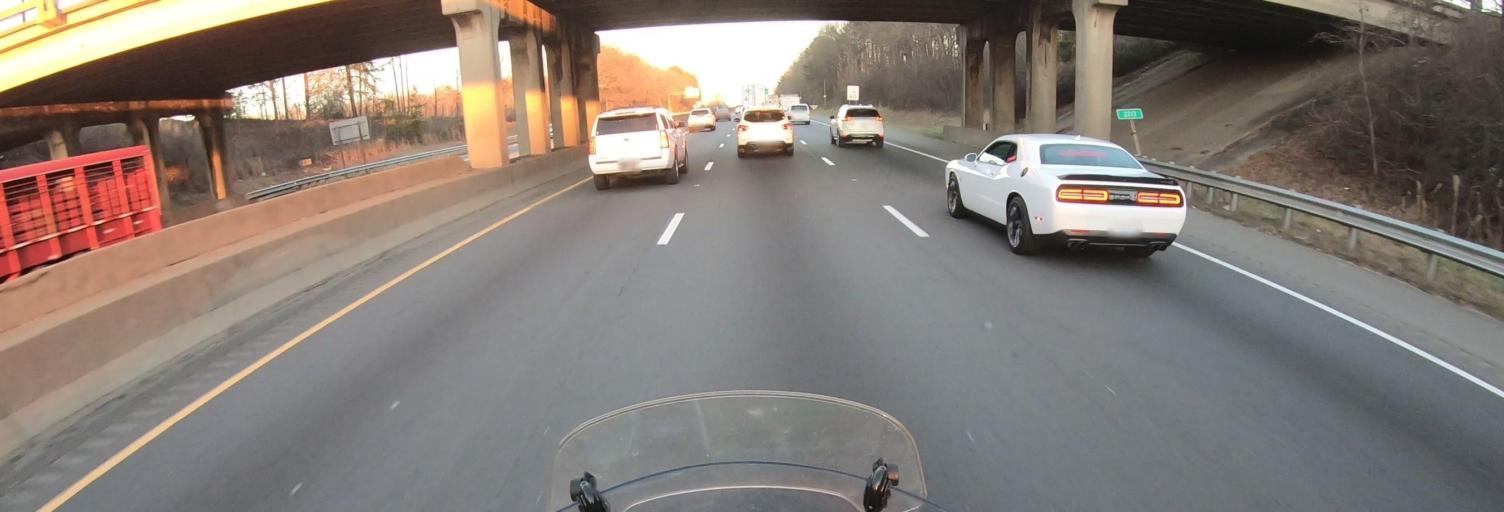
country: US
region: North Carolina
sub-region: Gaston County
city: Lowell
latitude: 35.2619
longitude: -81.0987
